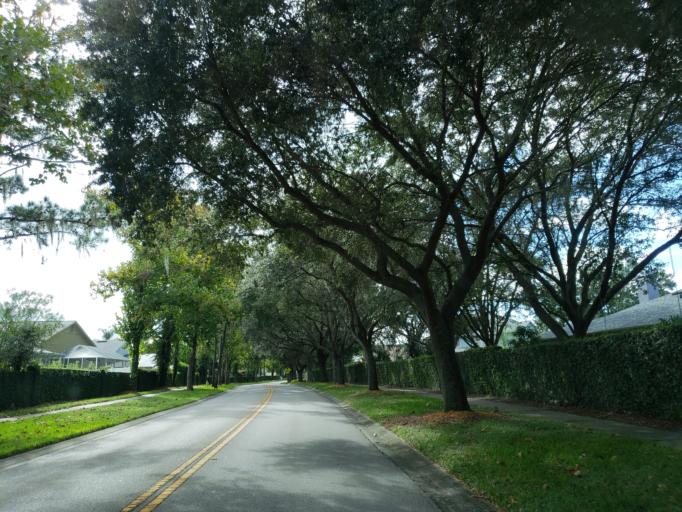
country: US
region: Florida
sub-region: Hillsborough County
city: Bloomingdale
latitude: 27.8740
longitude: -82.2500
